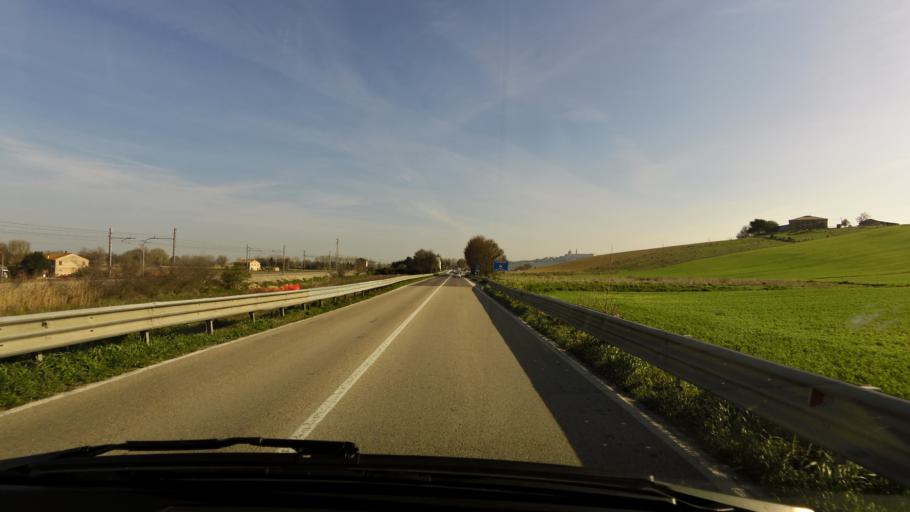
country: IT
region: The Marches
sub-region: Provincia di Ancona
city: Villa Musone
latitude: 43.4687
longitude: 13.6002
